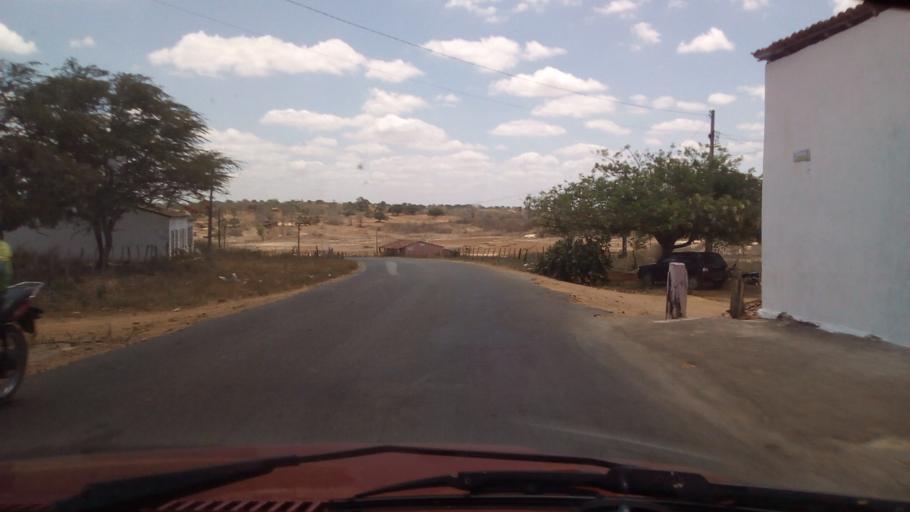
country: BR
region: Paraiba
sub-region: Cacimba De Dentro
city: Cacimba de Dentro
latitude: -6.6116
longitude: -35.8073
